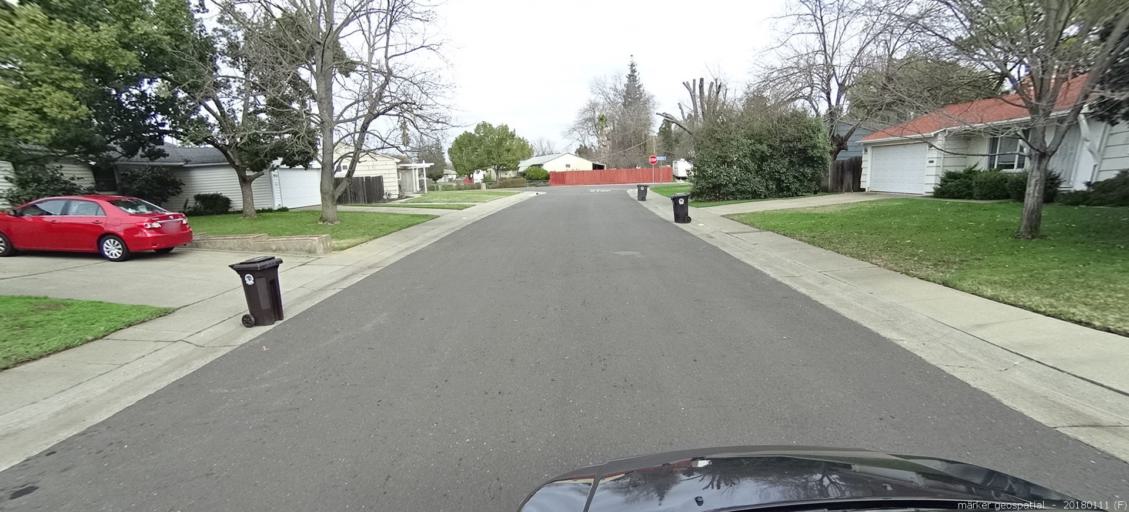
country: US
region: California
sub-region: Sacramento County
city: Rancho Cordova
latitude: 38.6112
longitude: -121.2970
